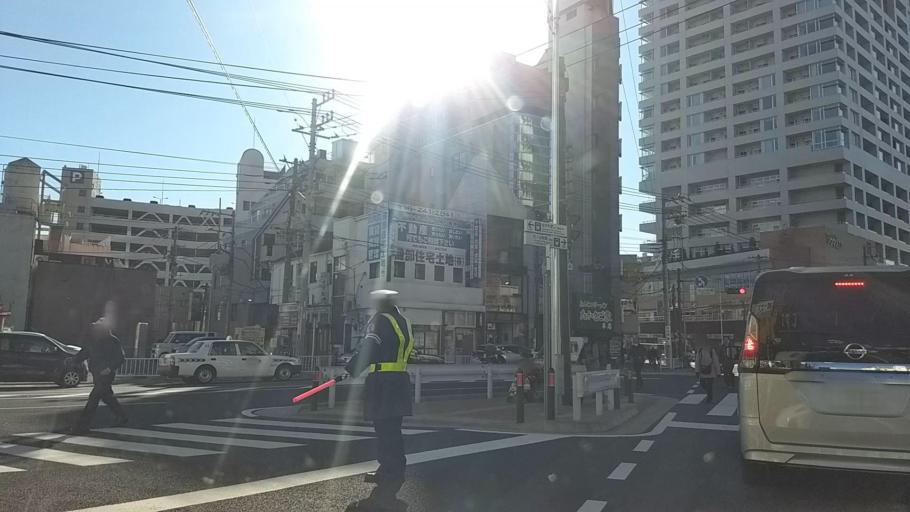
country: JP
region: Kanagawa
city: Yokohama
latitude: 35.4464
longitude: 139.6274
